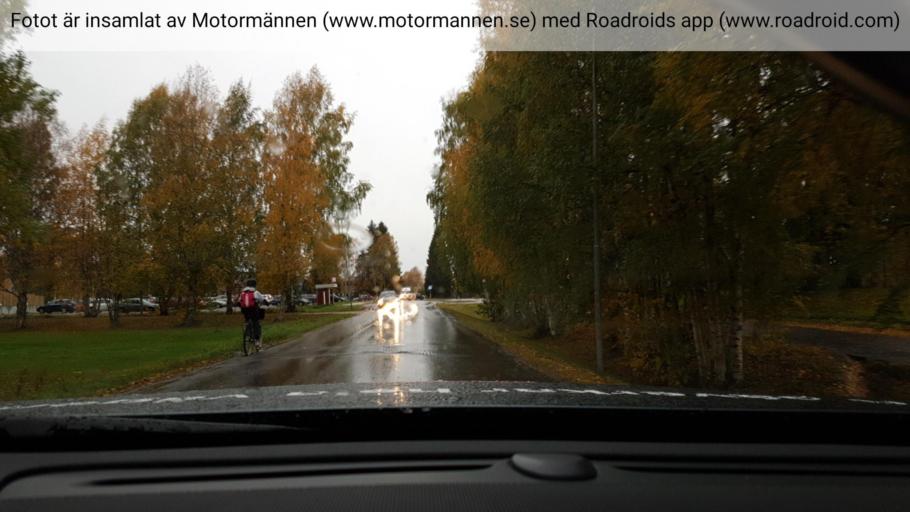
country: SE
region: Norrbotten
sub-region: Lulea Kommun
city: Sodra Sunderbyn
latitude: 65.6587
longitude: 21.9491
